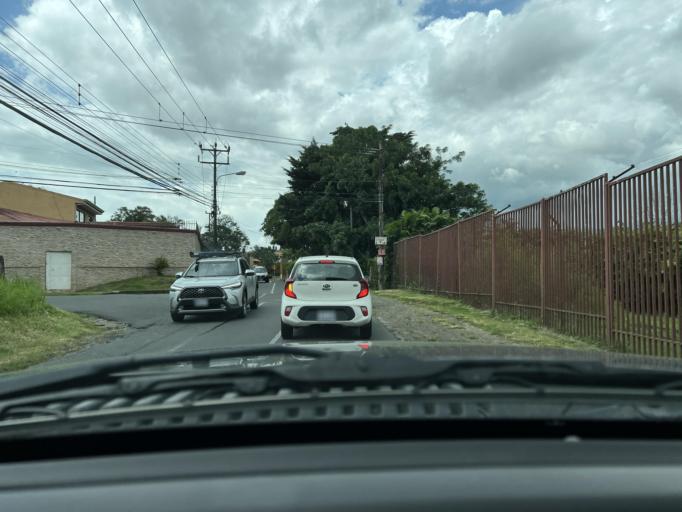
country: CR
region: San Jose
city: Granadilla
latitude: 9.9341
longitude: -84.0296
